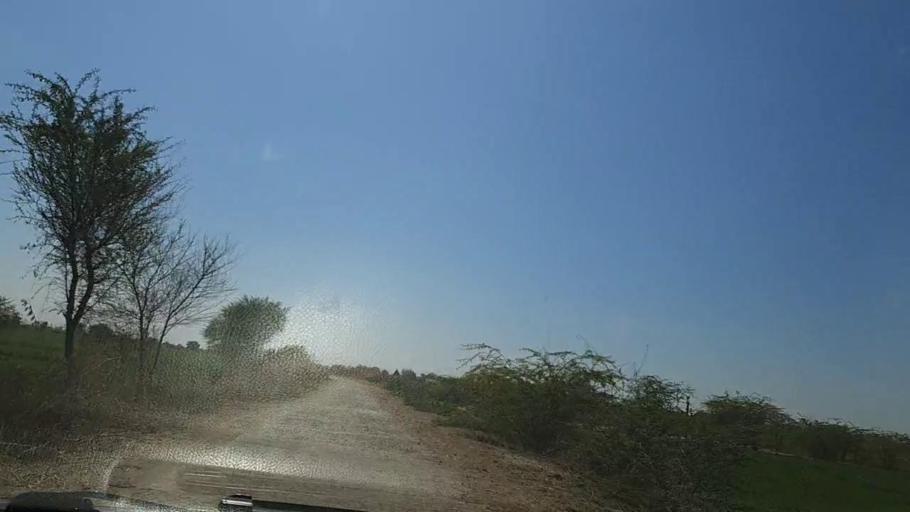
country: PK
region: Sindh
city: Dhoro Naro
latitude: 25.4855
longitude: 69.5428
